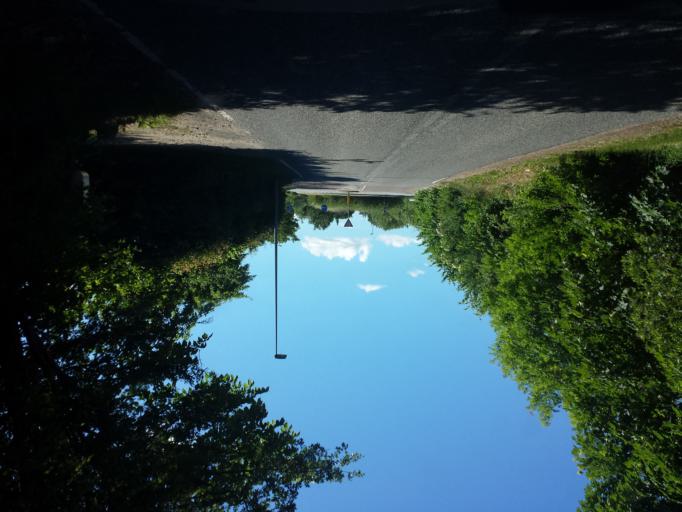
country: DK
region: Capital Region
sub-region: Egedal Kommune
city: Ganlose
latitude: 55.7981
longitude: 12.2638
